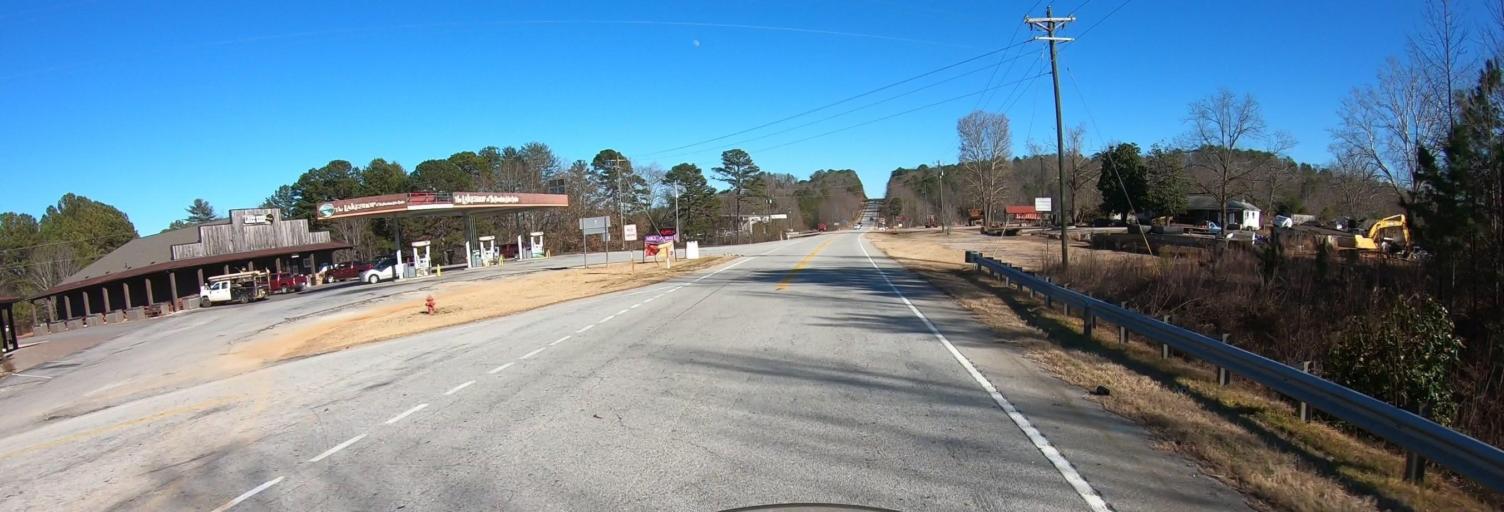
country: US
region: South Carolina
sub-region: Oconee County
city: Walhalla
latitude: 34.9127
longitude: -82.9367
